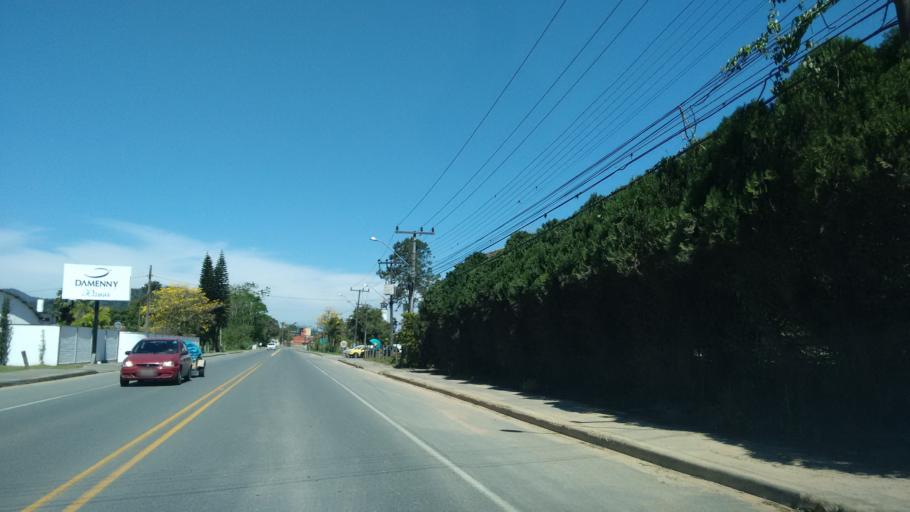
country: BR
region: Santa Catarina
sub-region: Pomerode
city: Pomerode
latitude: -26.7607
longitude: -49.1706
